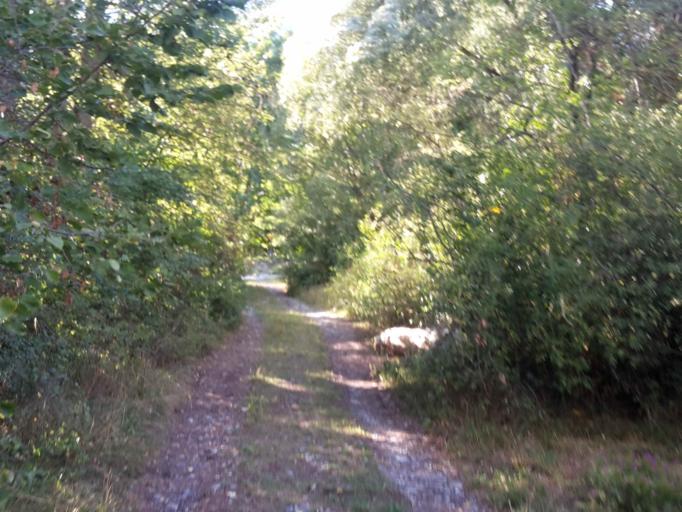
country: FR
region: Provence-Alpes-Cote d'Azur
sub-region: Departement des Hautes-Alpes
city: Embrun
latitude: 44.5542
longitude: 6.4880
